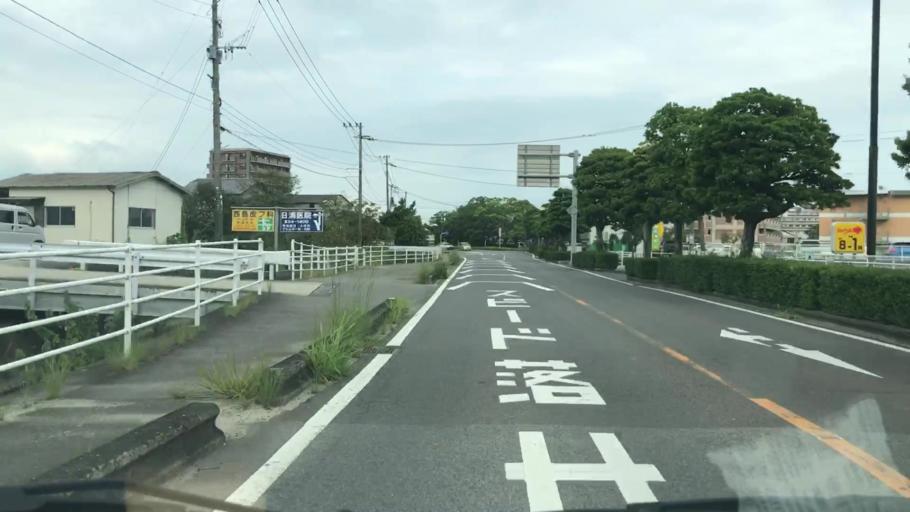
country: JP
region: Saga Prefecture
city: Saga-shi
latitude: 33.2765
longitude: 130.2617
